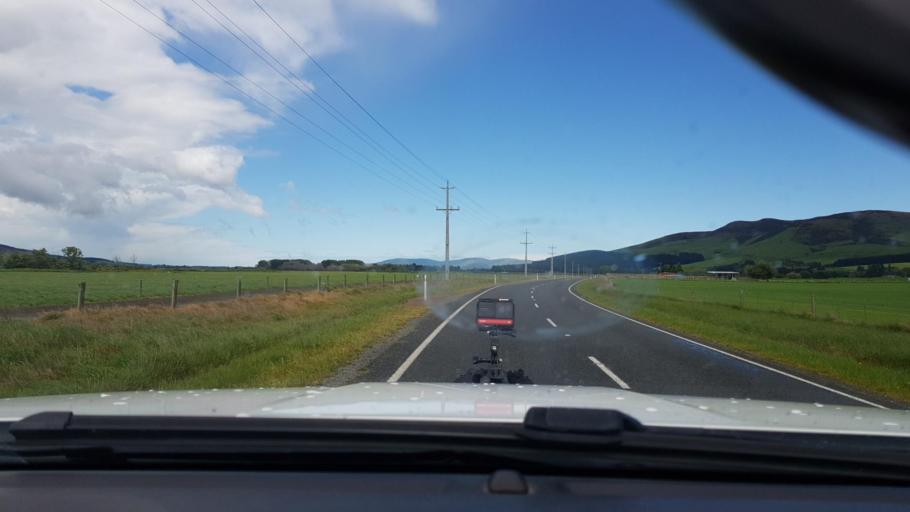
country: NZ
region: Southland
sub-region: Southland District
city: Winton
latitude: -45.7885
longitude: 168.3895
